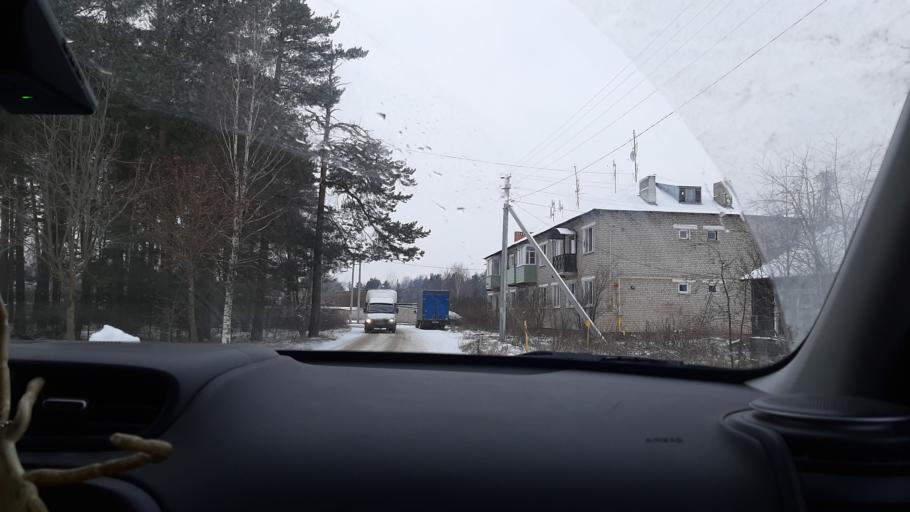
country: RU
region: Ivanovo
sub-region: Gorod Ivanovo
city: Ivanovo
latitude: 56.9262
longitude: 40.9826
